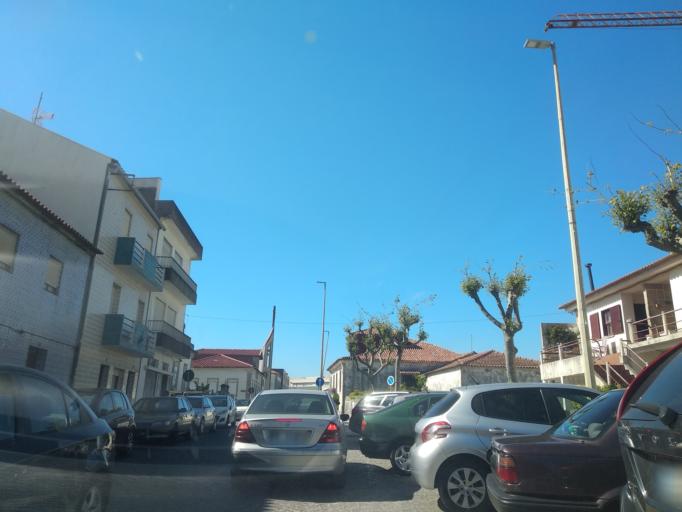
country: PT
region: Braga
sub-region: Esposende
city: Apulia
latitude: 41.4840
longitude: -8.7771
